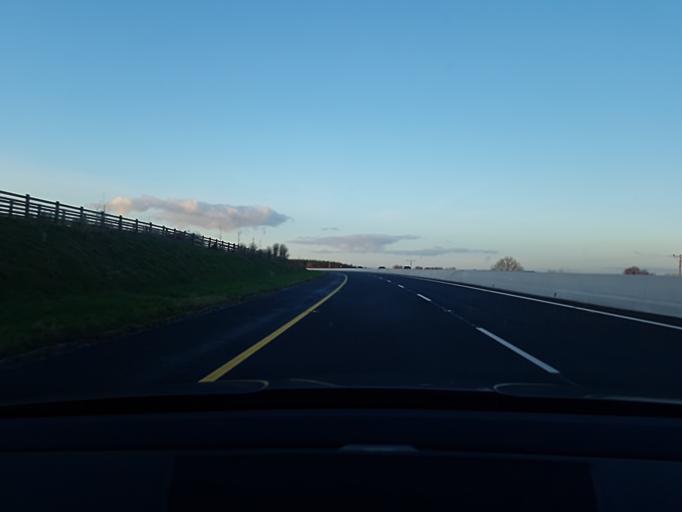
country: IE
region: Connaught
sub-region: County Galway
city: Tuam
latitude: 53.4848
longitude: -8.8635
